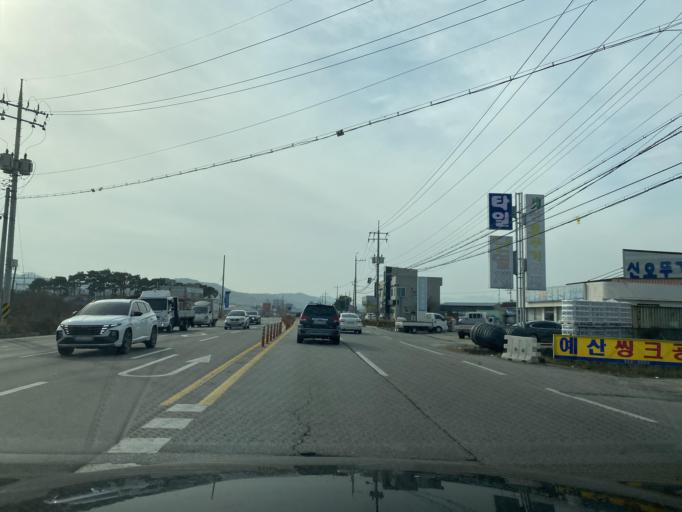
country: KR
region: Chungcheongnam-do
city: Yesan
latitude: 36.6905
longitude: 126.8277
